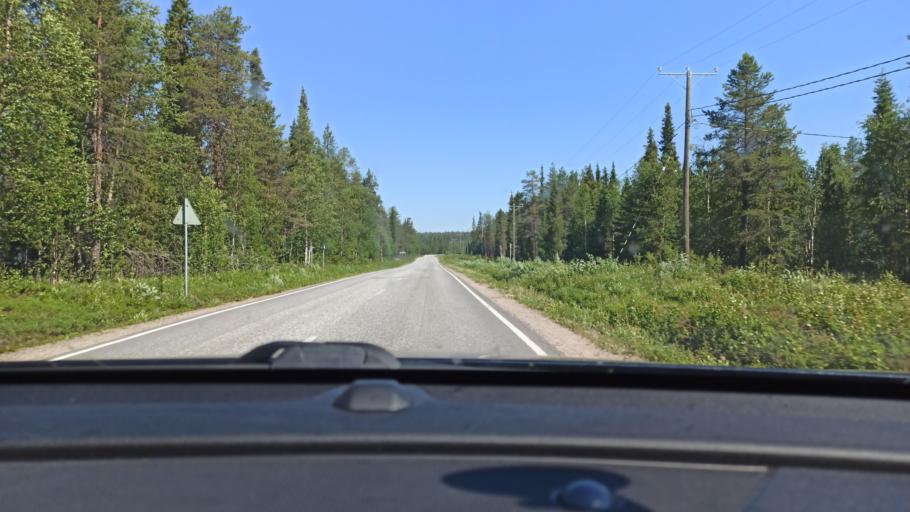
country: FI
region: Lapland
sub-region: Tunturi-Lappi
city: Kolari
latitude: 67.6260
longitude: 24.1554
